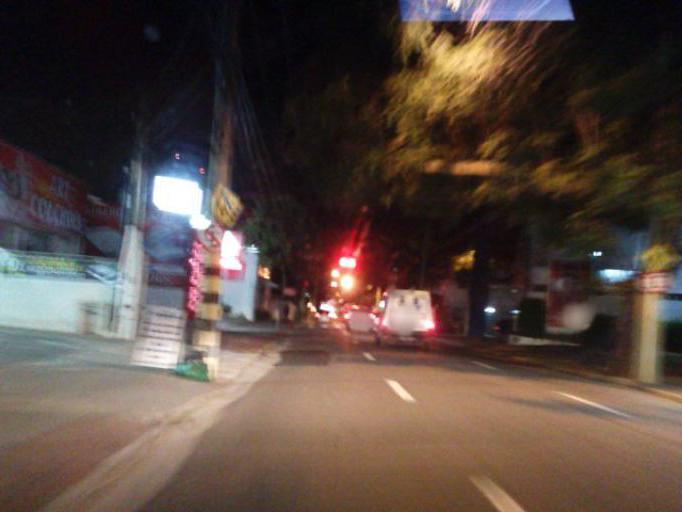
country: BR
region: Sao Paulo
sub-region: Sao Jose Dos Campos
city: Sao Jose dos Campos
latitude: -23.2029
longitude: -45.9002
